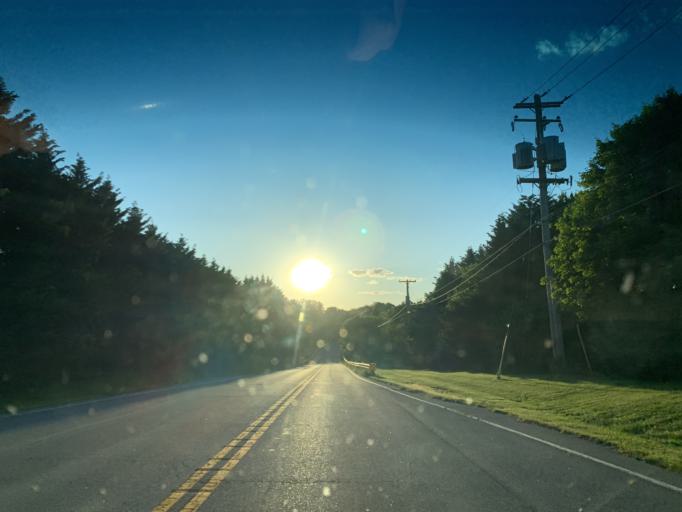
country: US
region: Maryland
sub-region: Cecil County
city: Elkton
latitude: 39.7137
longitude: -75.8732
